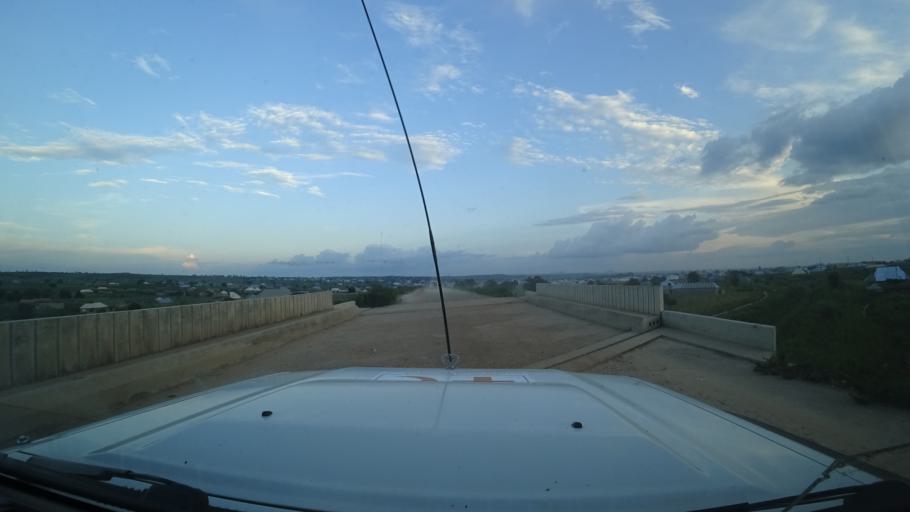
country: NG
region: Niger
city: Minna
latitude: 9.6517
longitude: 6.5777
